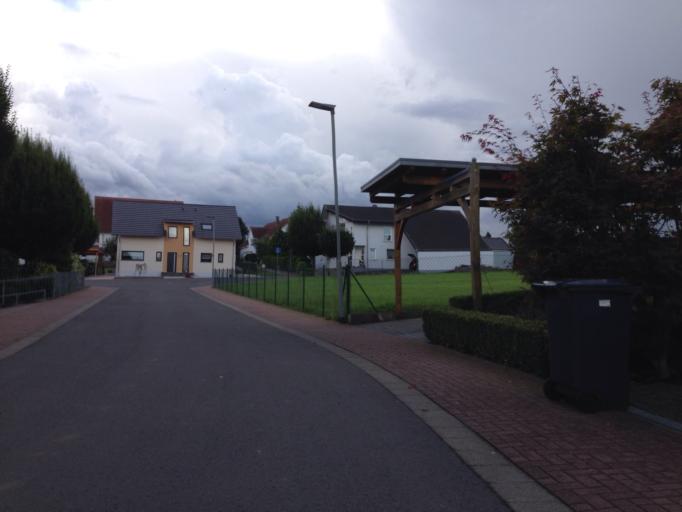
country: DE
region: Hesse
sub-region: Regierungsbezirk Giessen
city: Hungen
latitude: 50.4749
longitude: 8.8860
